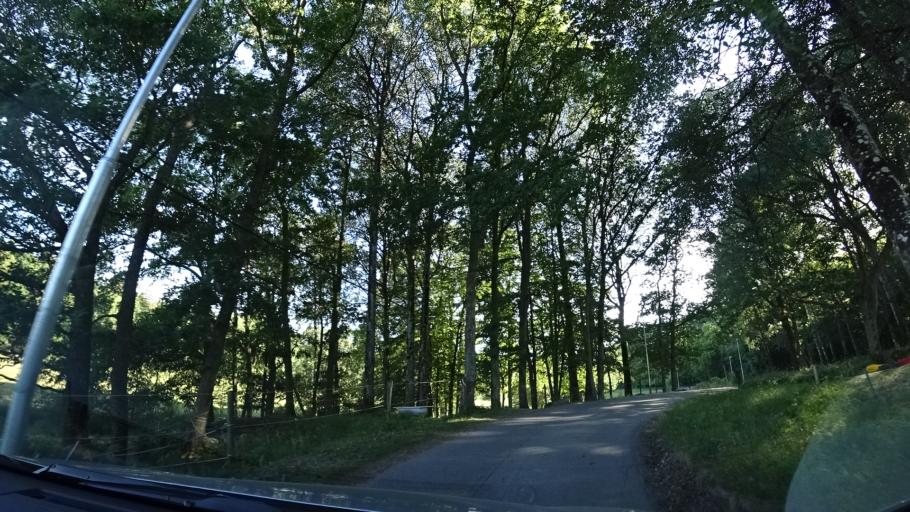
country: SE
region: Vaestra Goetaland
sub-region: Goteborg
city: Billdal
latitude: 57.5840
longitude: 11.9882
